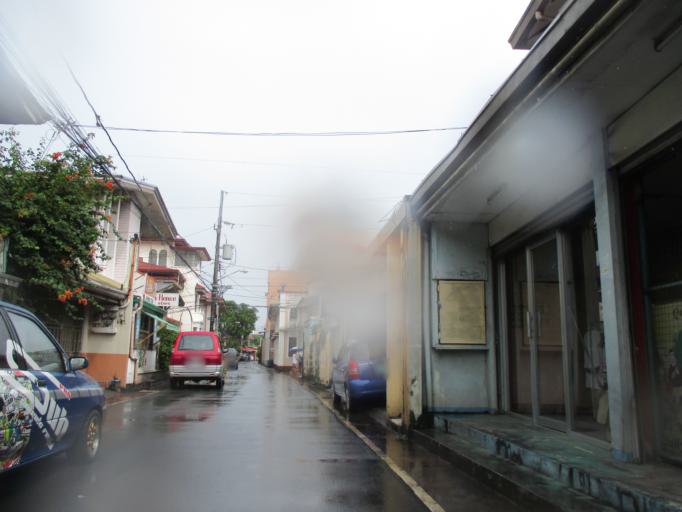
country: PH
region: Metro Manila
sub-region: Marikina
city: Calumpang
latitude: 14.6322
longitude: 121.0950
